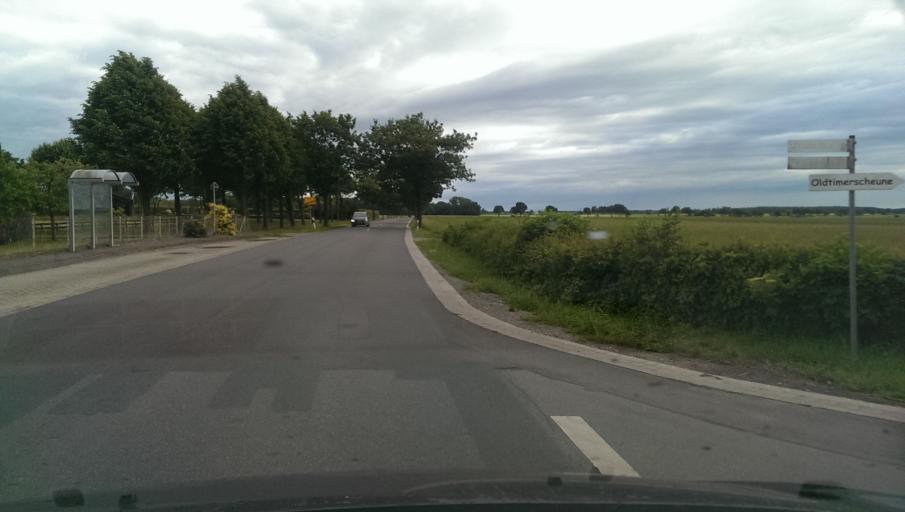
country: DE
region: Saxony-Anhalt
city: Jubar
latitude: 52.6715
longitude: 10.8525
